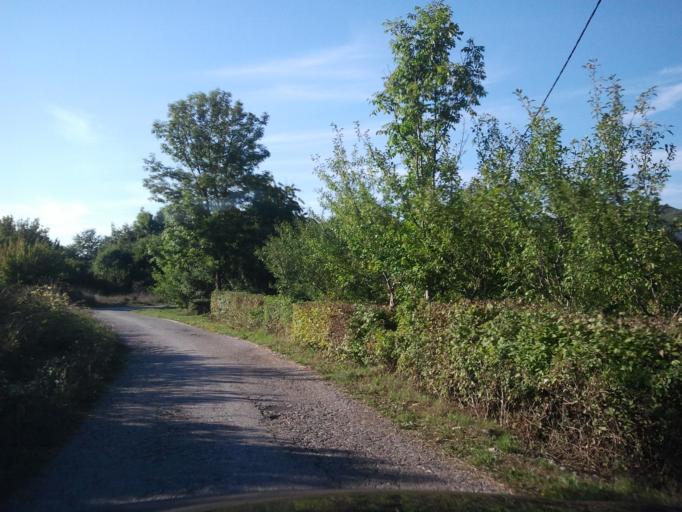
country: HR
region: Zadarska
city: Gracac
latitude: 44.3507
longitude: 15.7142
